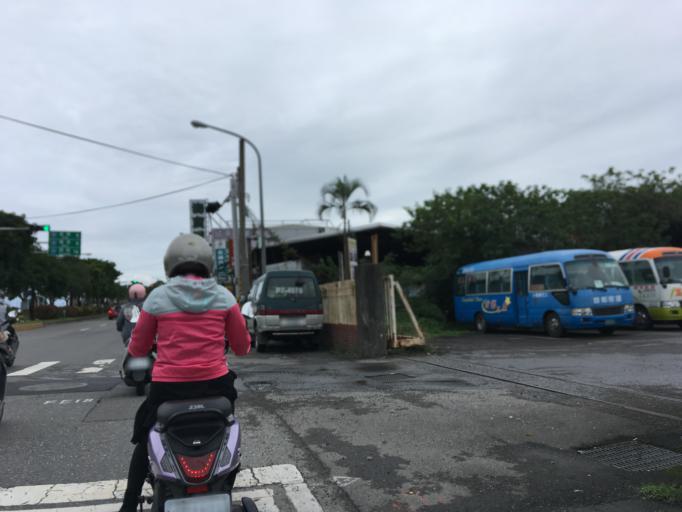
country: TW
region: Taiwan
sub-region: Yilan
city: Yilan
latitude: 24.7091
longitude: 121.7724
